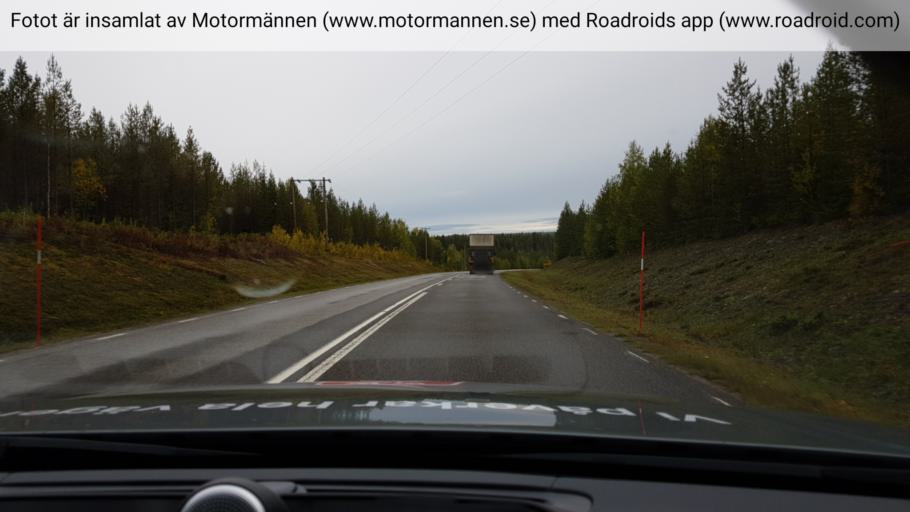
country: SE
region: Jaemtland
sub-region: Stroemsunds Kommun
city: Stroemsund
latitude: 64.2364
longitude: 15.4585
